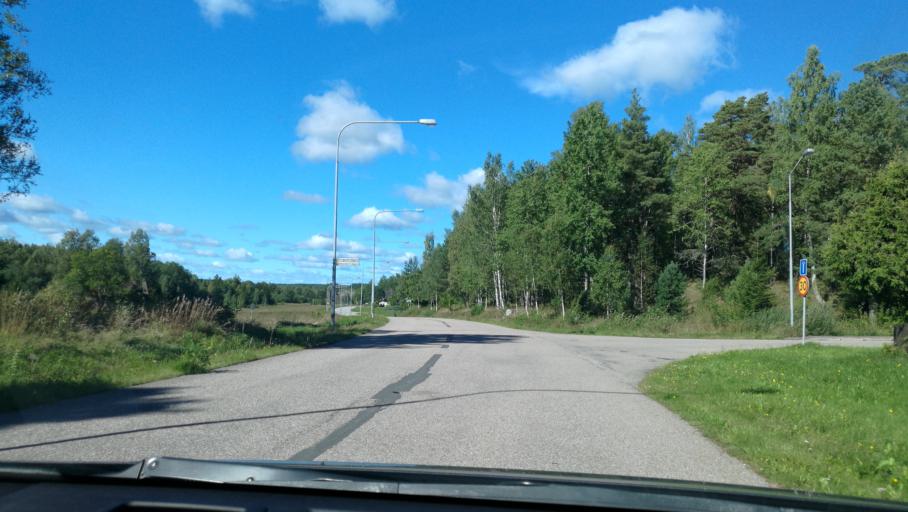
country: SE
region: Vaestmanland
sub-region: Surahammars Kommun
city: Surahammar
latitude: 59.6924
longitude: 16.2348
